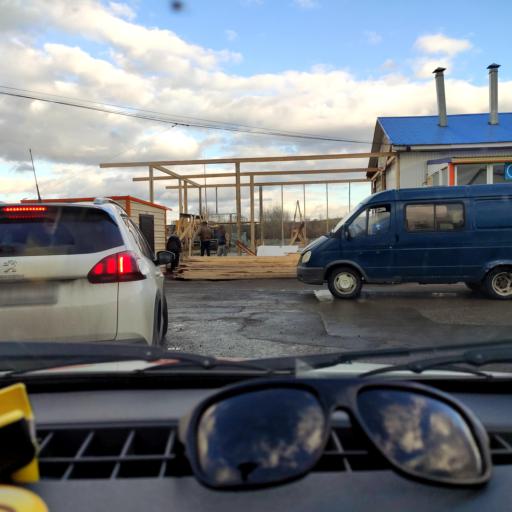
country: RU
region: Bashkortostan
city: Ufa
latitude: 54.7643
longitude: 55.9416
